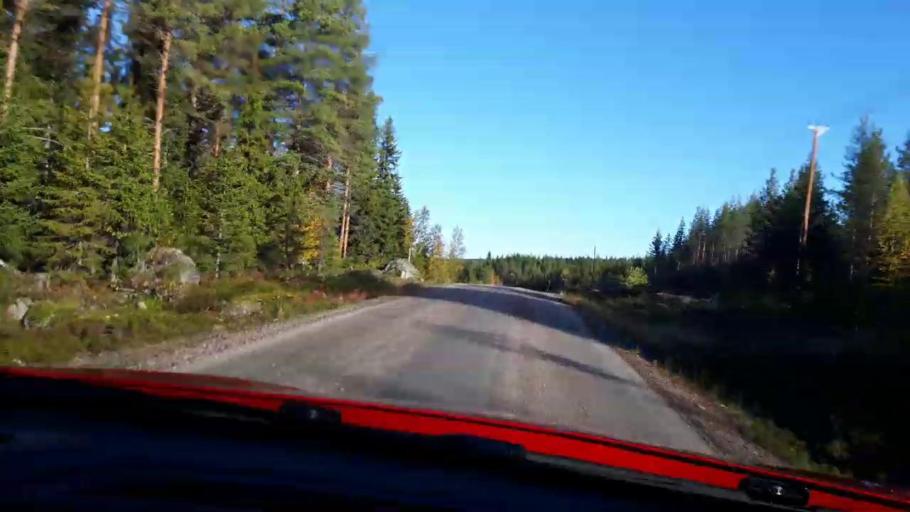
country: SE
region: Jaemtland
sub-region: Stroemsunds Kommun
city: Stroemsund
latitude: 64.3694
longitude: 15.1582
